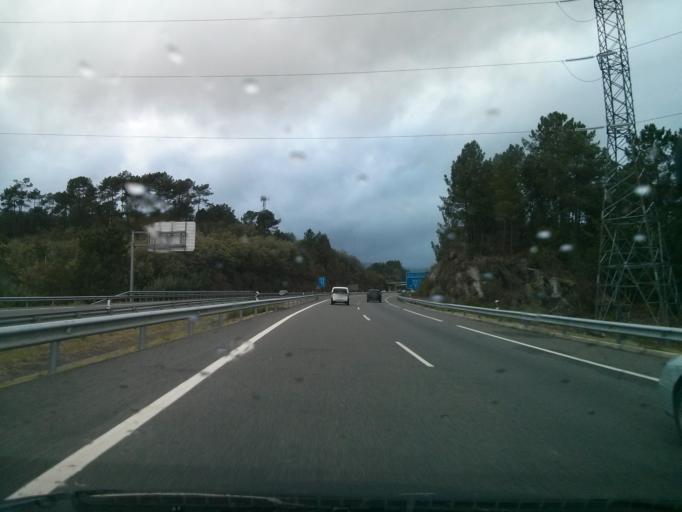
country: ES
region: Galicia
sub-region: Provincia de Ourense
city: Ribadavia
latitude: 42.3015
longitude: -8.1370
